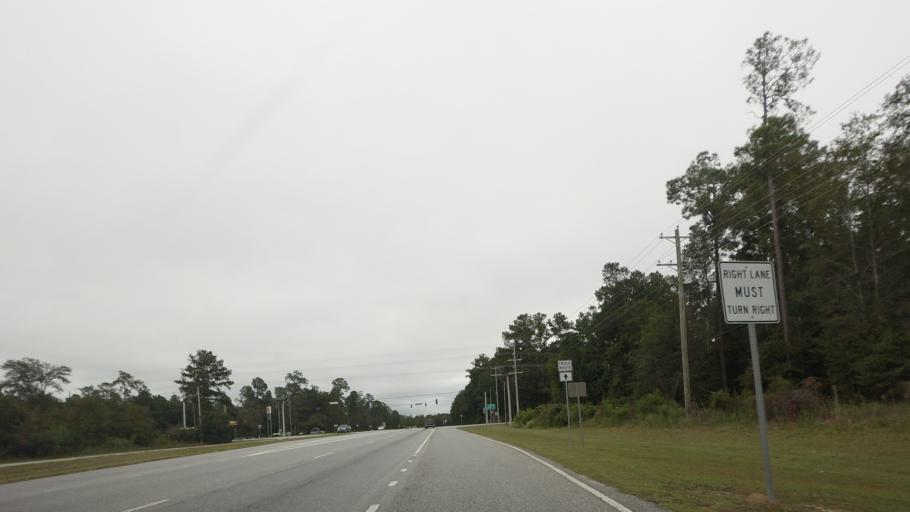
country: US
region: Georgia
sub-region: Lowndes County
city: Valdosta
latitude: 30.8760
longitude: -83.2378
